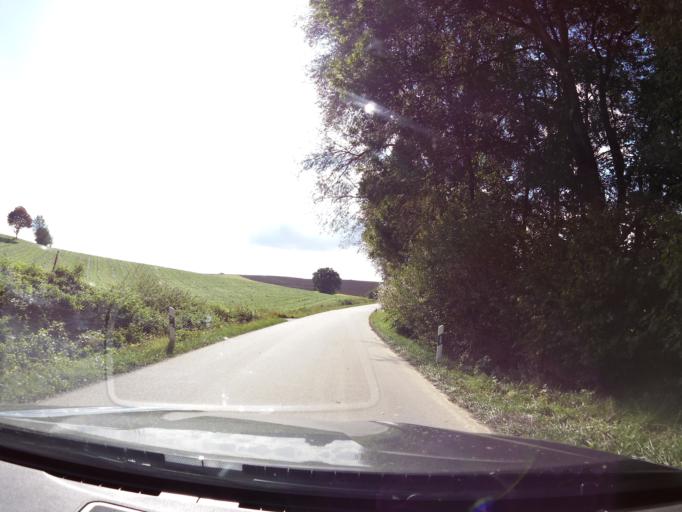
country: DE
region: Bavaria
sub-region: Lower Bavaria
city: Vilsheim
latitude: 48.4372
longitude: 12.1317
